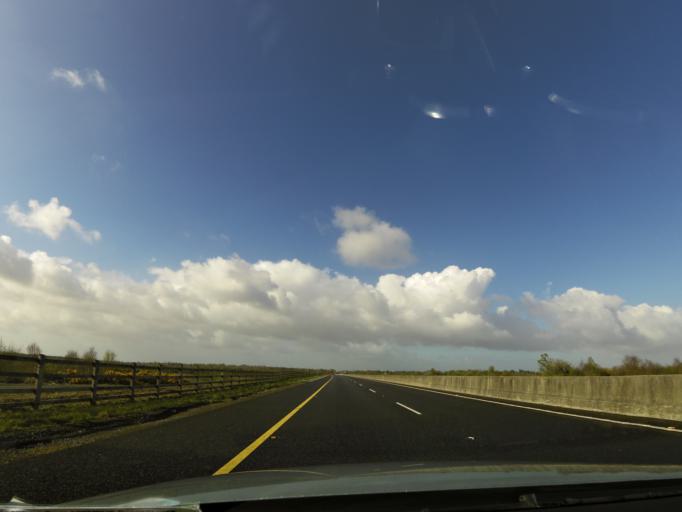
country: IE
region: Munster
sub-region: County Limerick
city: Castleconnell
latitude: 52.7209
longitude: -8.4697
